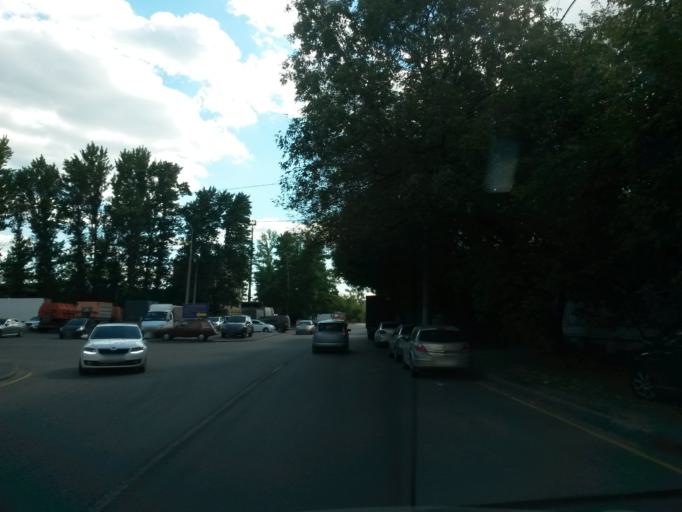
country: RU
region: Moskovskaya
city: Kozhukhovo
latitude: 55.7012
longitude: 37.6878
